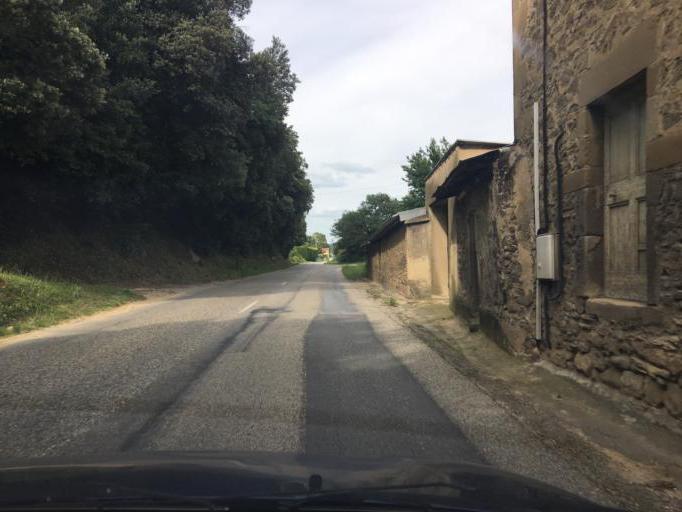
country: FR
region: Rhone-Alpes
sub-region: Departement de la Drome
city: Clerieux
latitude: 45.1124
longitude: 4.9591
